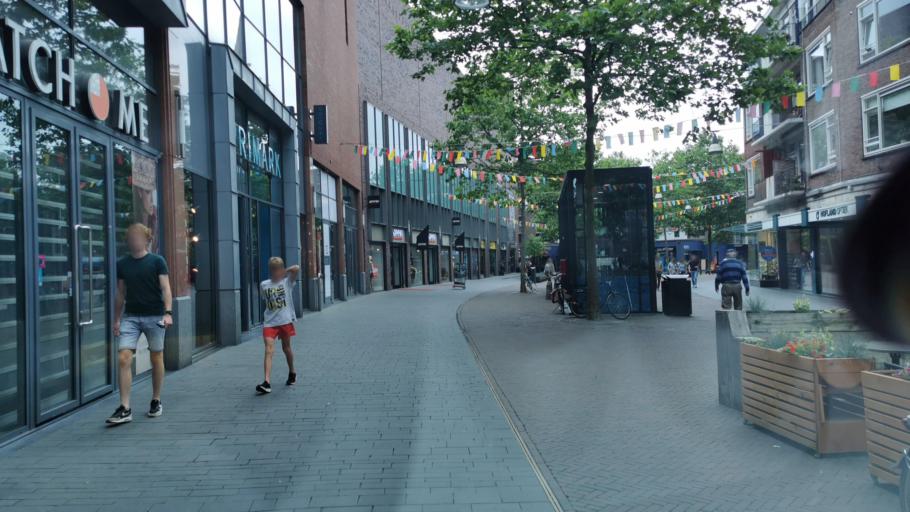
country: NL
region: Overijssel
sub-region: Gemeente Enschede
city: Enschede
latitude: 52.2181
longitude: 6.8961
